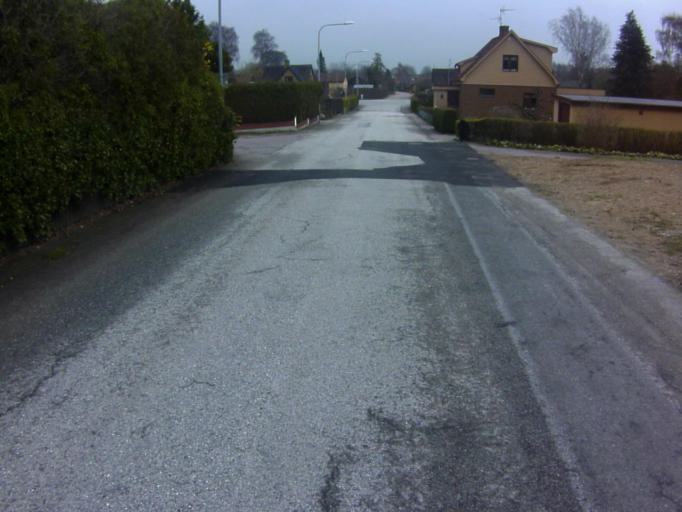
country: SE
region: Skane
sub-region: Kavlinge Kommun
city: Kaevlinge
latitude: 55.7730
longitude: 13.0833
